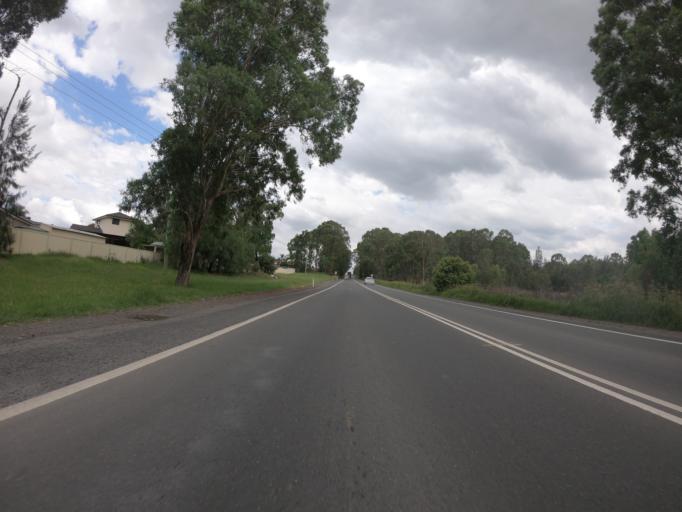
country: AU
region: New South Wales
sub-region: Blacktown
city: Mount Druitt
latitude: -33.8061
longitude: 150.7713
